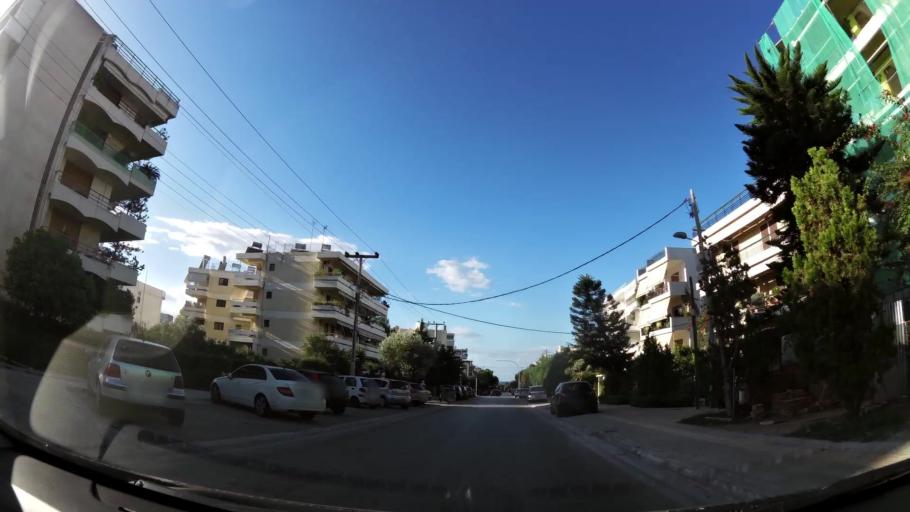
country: GR
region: Attica
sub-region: Nomarchia Athinas
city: Glyfada
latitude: 37.8713
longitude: 23.7510
